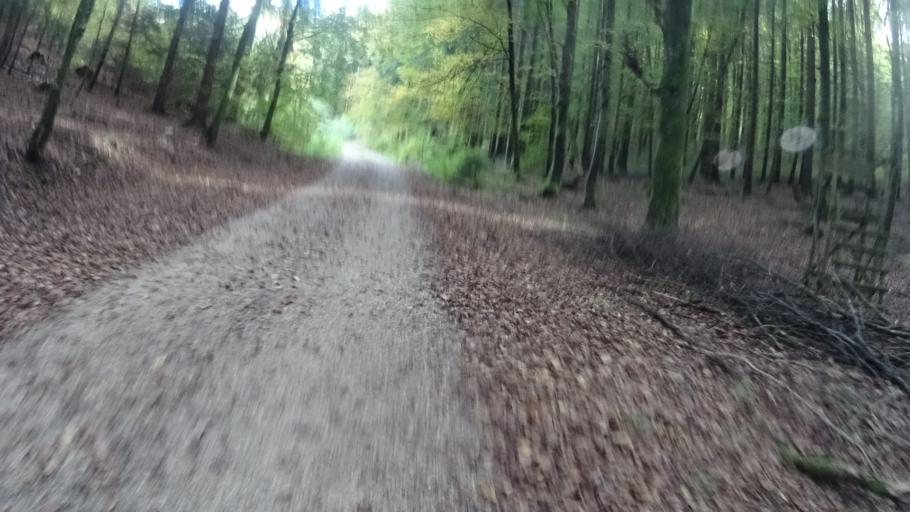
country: DE
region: Bavaria
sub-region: Upper Bavaria
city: Walting
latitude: 48.9014
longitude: 11.3175
